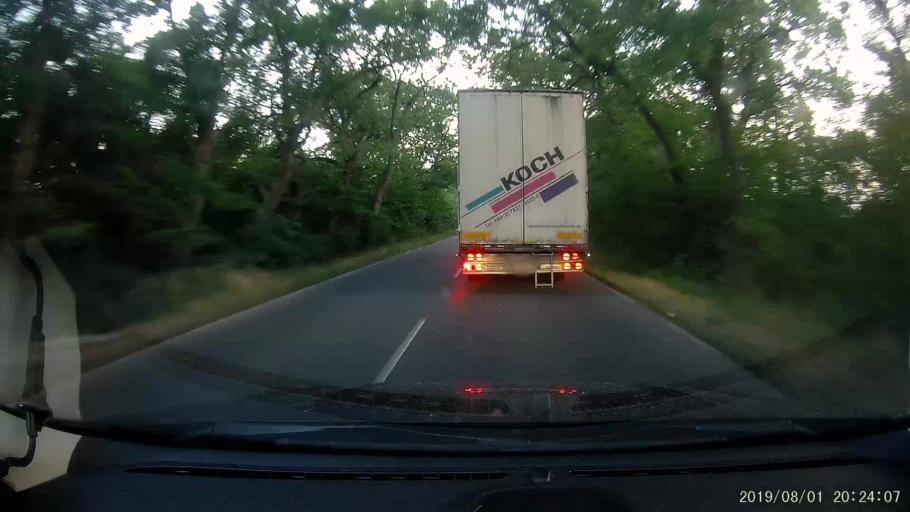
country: BG
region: Yambol
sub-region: Obshtina Elkhovo
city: Elkhovo
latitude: 42.2372
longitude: 26.5958
